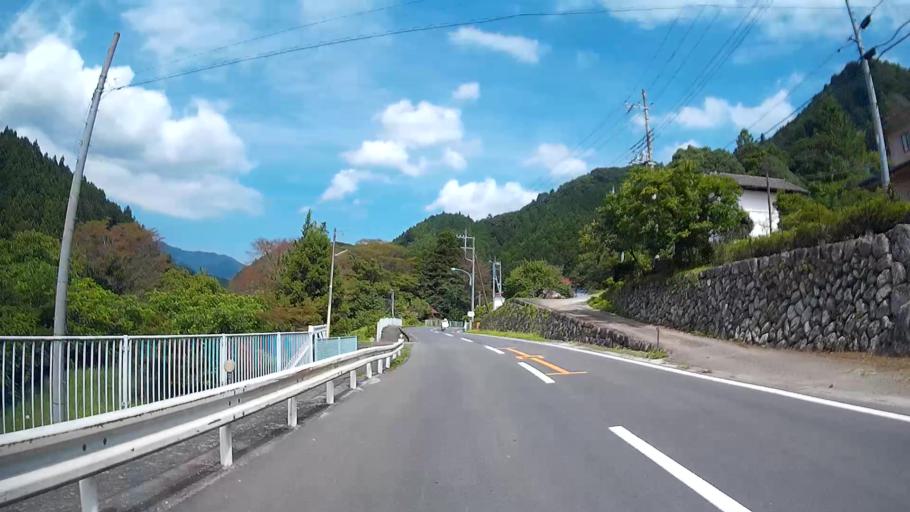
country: JP
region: Tokyo
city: Ome
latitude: 35.8929
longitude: 139.1776
